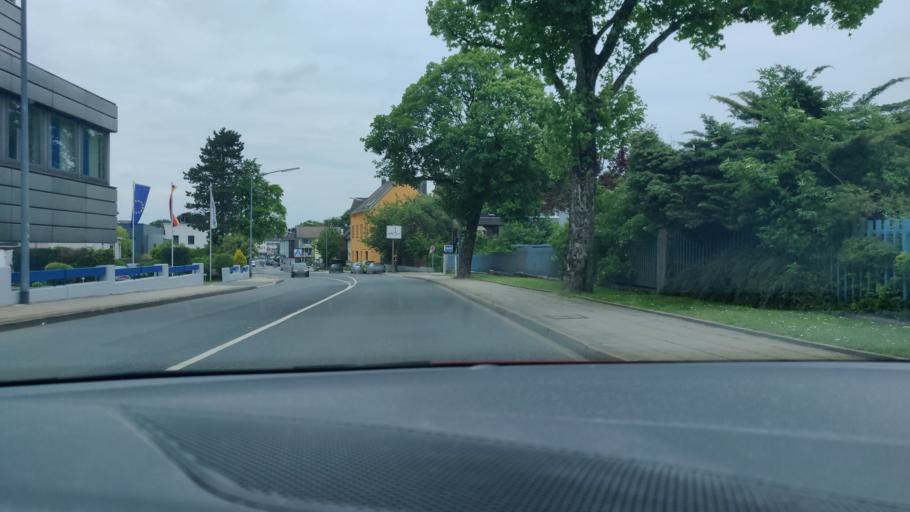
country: DE
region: North Rhine-Westphalia
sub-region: Regierungsbezirk Dusseldorf
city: Velbert
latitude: 51.3103
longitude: 7.0670
